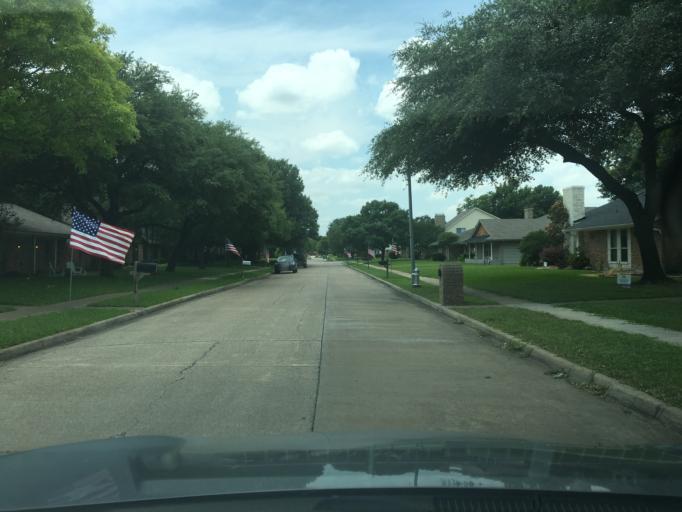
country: US
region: Texas
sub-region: Dallas County
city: Richardson
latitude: 32.9566
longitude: -96.6896
